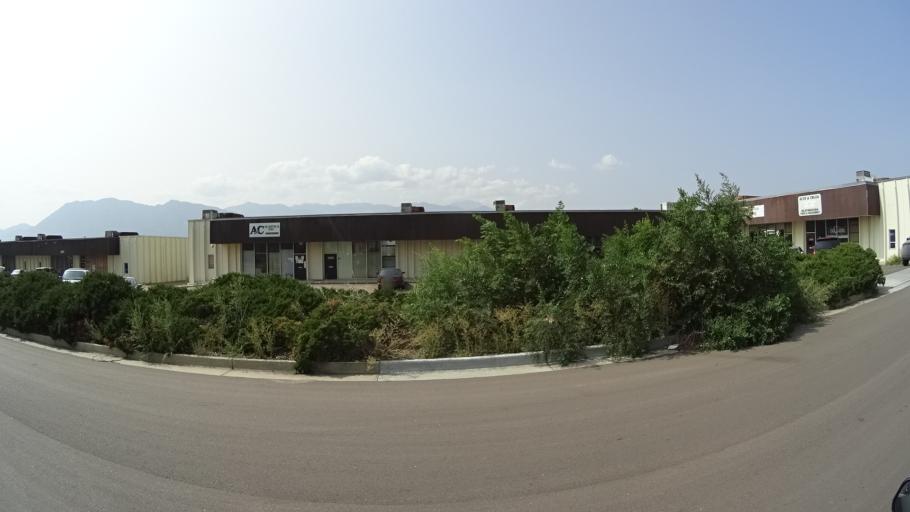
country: US
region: Colorado
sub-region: El Paso County
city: Stratmoor
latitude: 38.7952
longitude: -104.7732
